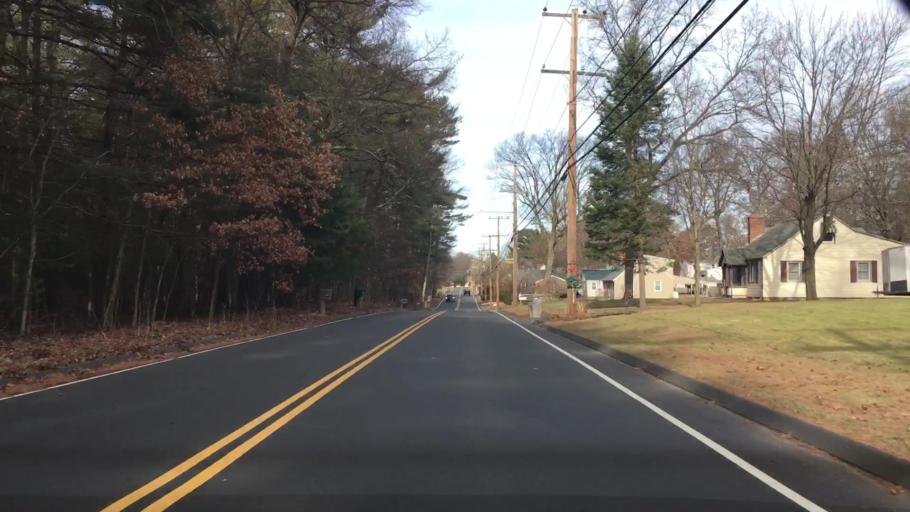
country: US
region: Connecticut
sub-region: Hartford County
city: Plainville
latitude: 41.6637
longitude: -72.9019
